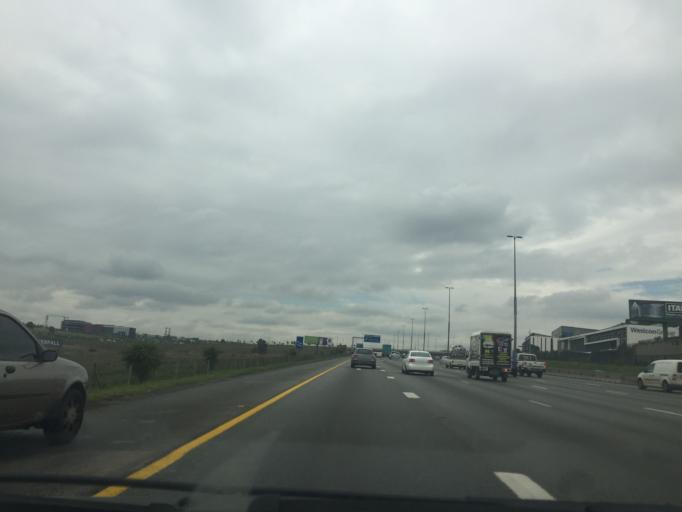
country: ZA
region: Gauteng
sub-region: City of Johannesburg Metropolitan Municipality
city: Midrand
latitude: -26.0245
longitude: 28.1111
